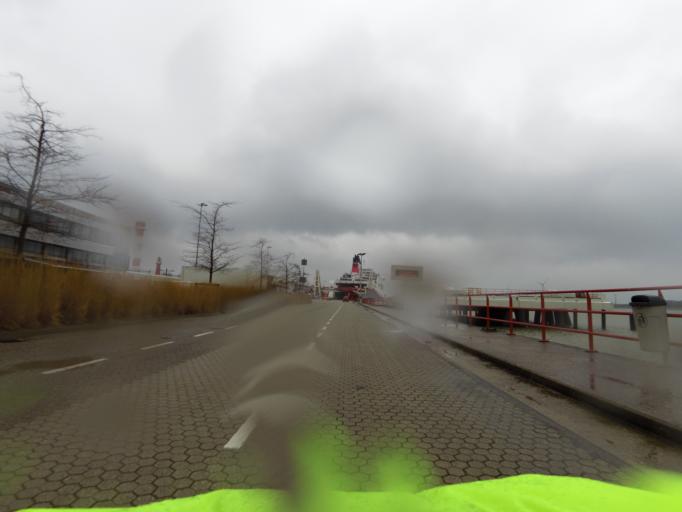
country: NL
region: South Holland
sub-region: Gemeente Rotterdam
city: Hoek van Holland
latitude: 51.9746
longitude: 4.1283
